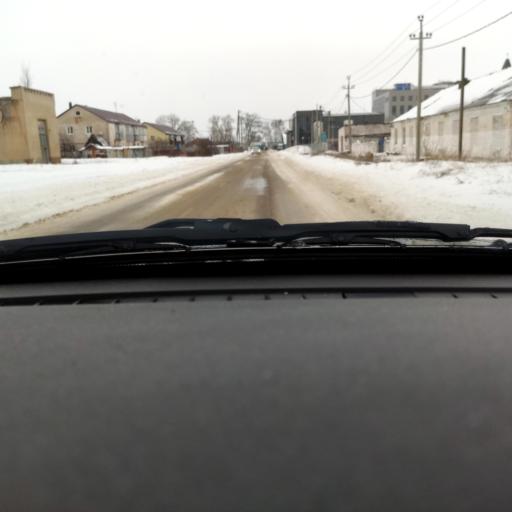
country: RU
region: Voronezj
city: Maslovka
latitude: 51.5368
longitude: 39.3430
